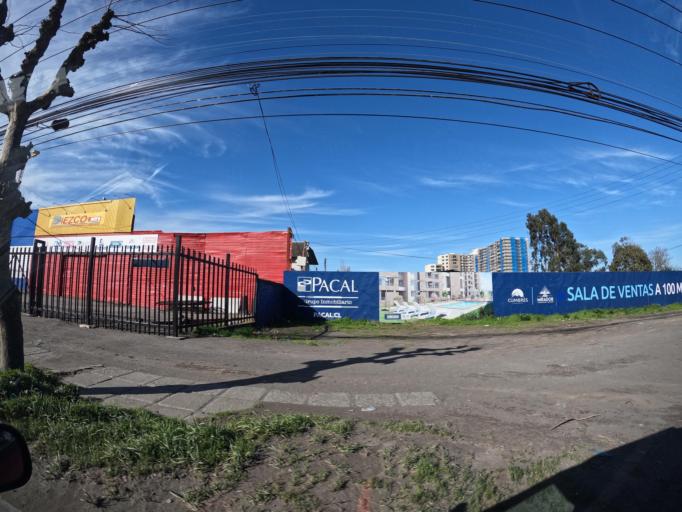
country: CL
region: Biobio
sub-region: Provincia de Concepcion
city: Concepcion
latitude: -36.7934
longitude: -73.0866
